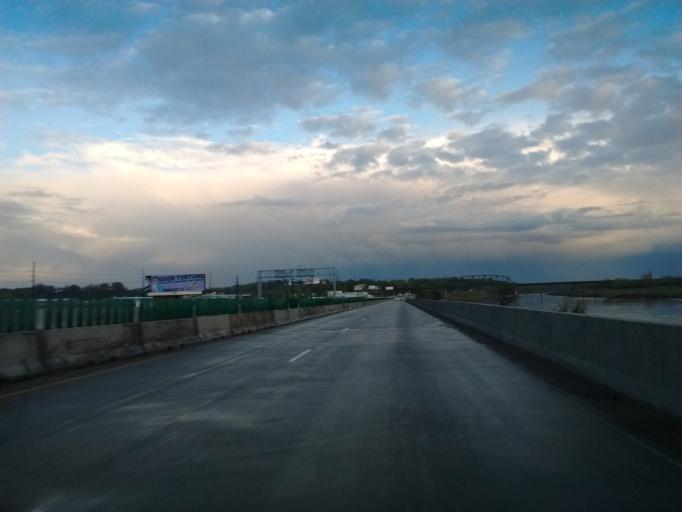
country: US
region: Iowa
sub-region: Woodbury County
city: Sioux City
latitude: 42.4841
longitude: -96.3920
